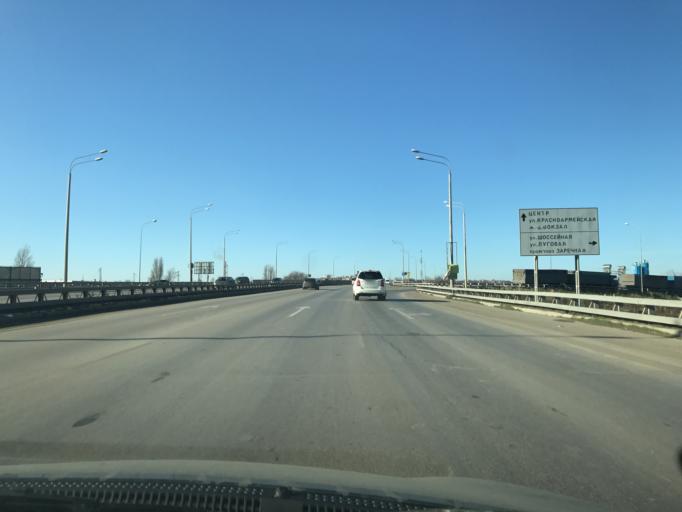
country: RU
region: Rostov
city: Rostov-na-Donu
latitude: 47.2028
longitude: 39.7133
